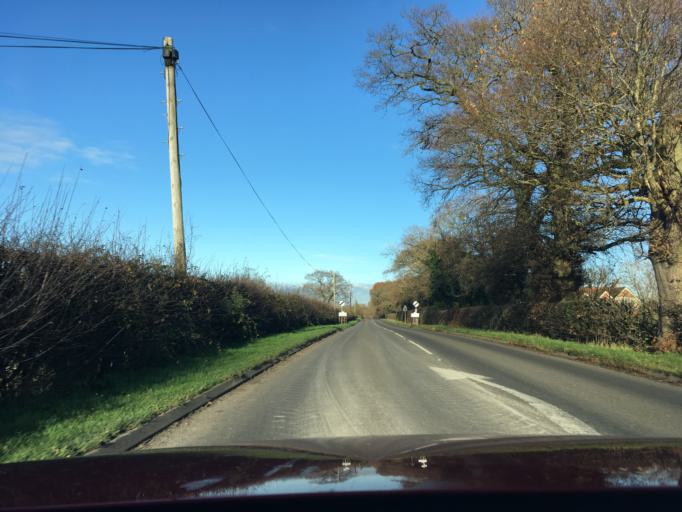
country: GB
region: England
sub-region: Staffordshire
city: Barton under Needwood
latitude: 52.8074
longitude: -1.7371
